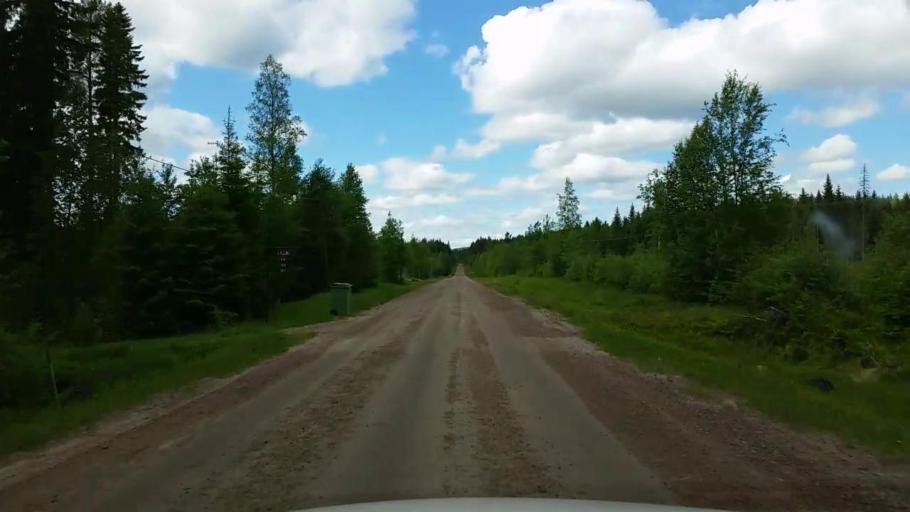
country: SE
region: Gaevleborg
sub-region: Ovanakers Kommun
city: Alfta
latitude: 61.4862
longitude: 15.9890
